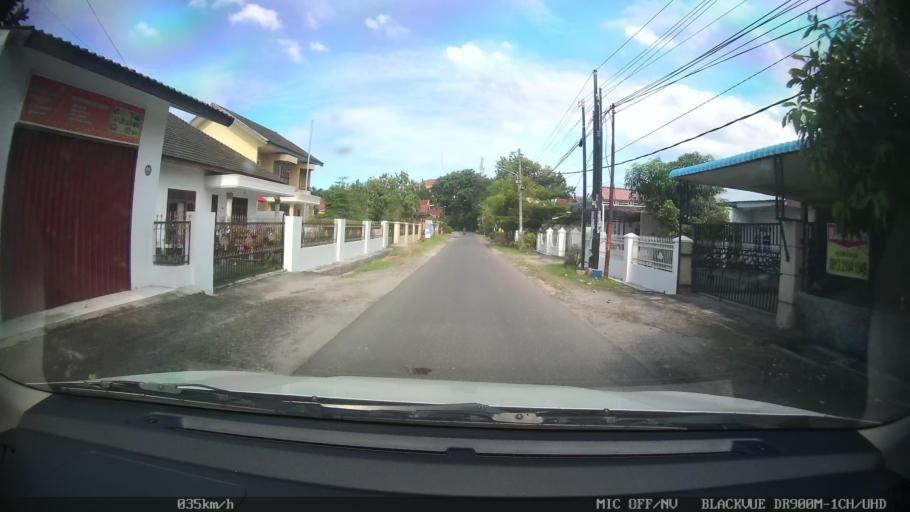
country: ID
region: North Sumatra
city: Medan
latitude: 3.6150
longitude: 98.6618
